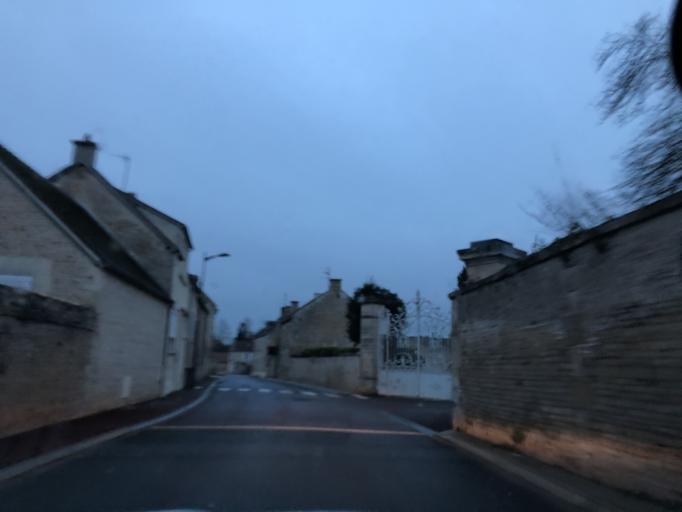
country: FR
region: Lower Normandy
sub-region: Departement du Calvados
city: Mathieu
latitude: 49.2536
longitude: -0.3682
